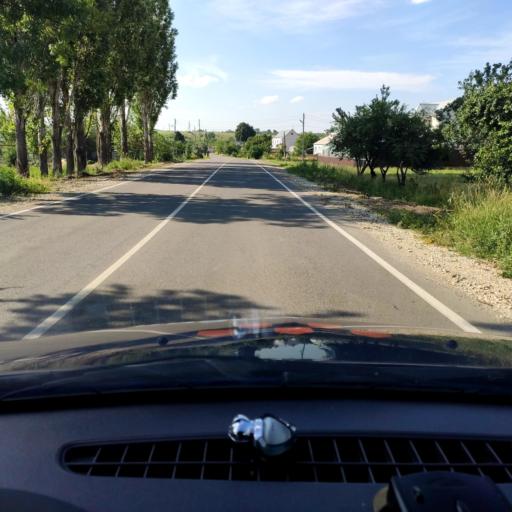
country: RU
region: Voronezj
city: Devitsa
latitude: 51.6529
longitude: 38.9722
